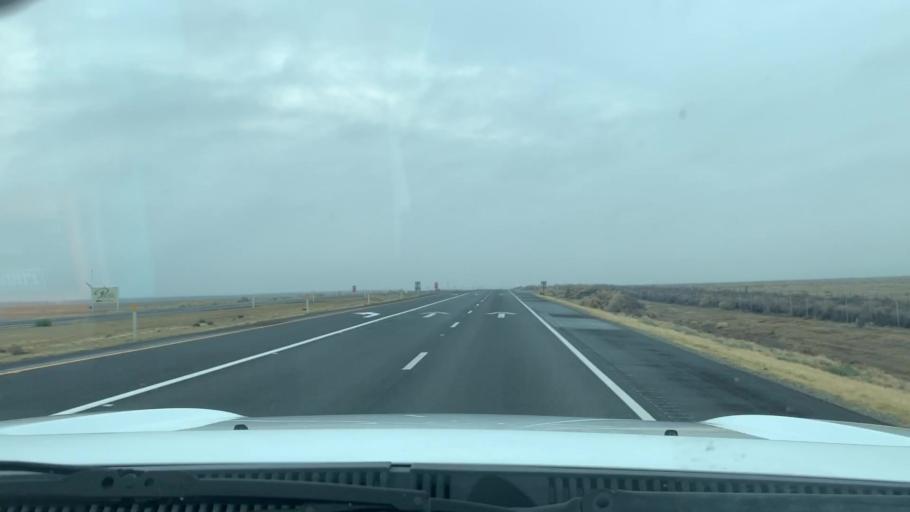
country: US
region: California
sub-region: Kern County
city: Lost Hills
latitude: 35.6327
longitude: -120.0029
